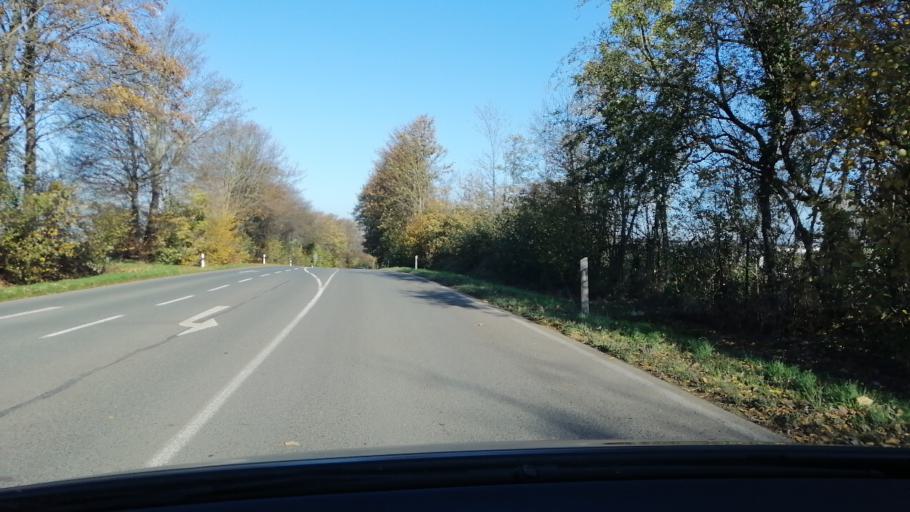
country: DE
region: North Rhine-Westphalia
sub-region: Regierungsbezirk Arnsberg
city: Frondenberg
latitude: 51.5214
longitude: 7.7698
